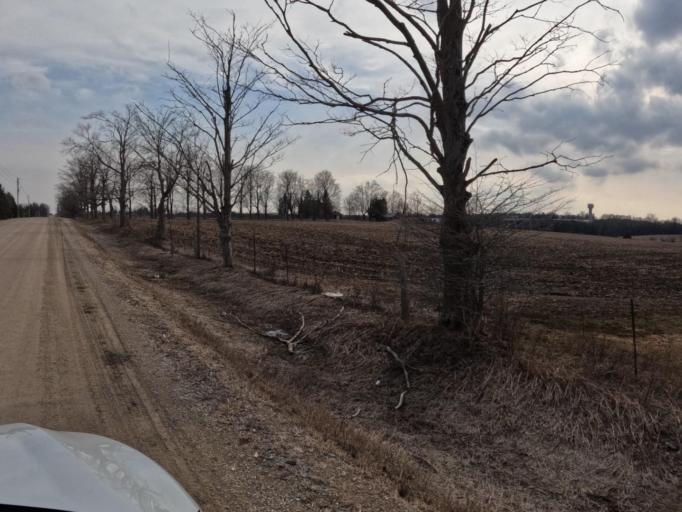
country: CA
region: Ontario
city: Shelburne
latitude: 43.9120
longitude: -80.3041
